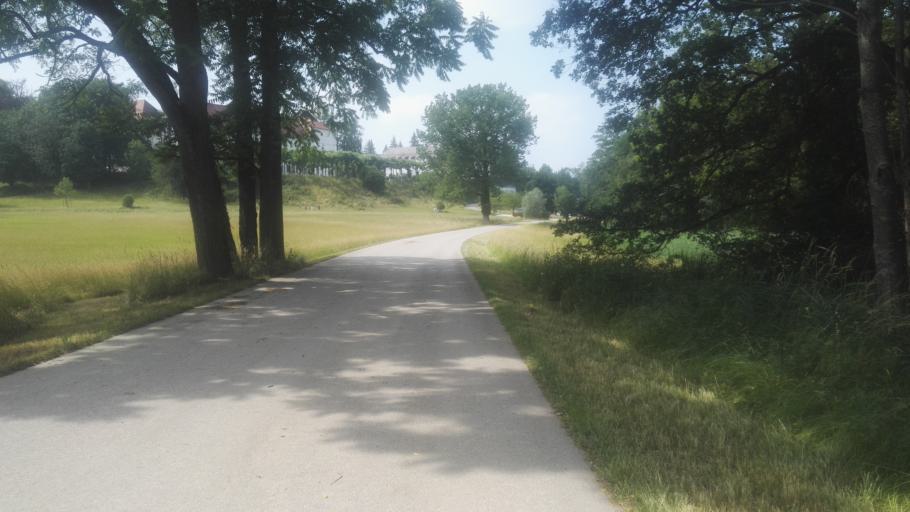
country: DE
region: Bavaria
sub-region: Upper Bavaria
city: Chiemsee
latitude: 47.8660
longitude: 12.3998
